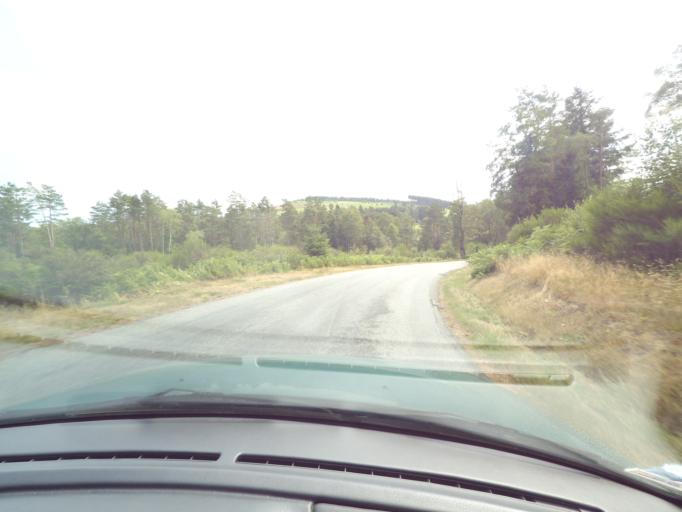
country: FR
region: Limousin
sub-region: Departement de la Correze
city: Bugeat
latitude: 45.7330
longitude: 1.9955
